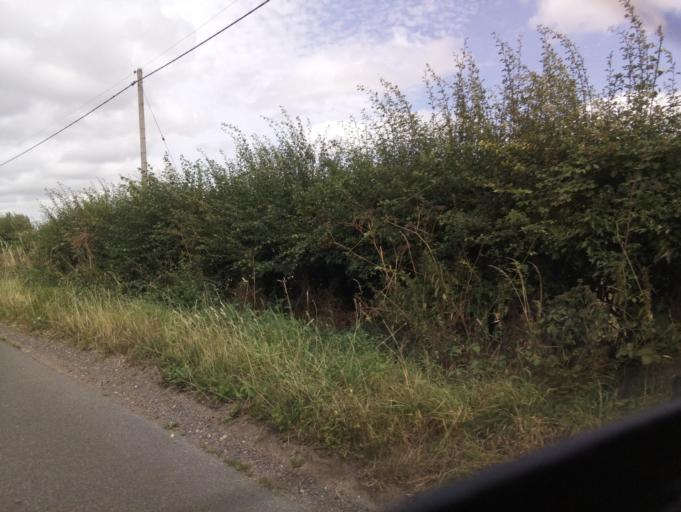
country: GB
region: England
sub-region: Warwickshire
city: Henley in Arden
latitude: 52.2823
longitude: -1.7579
